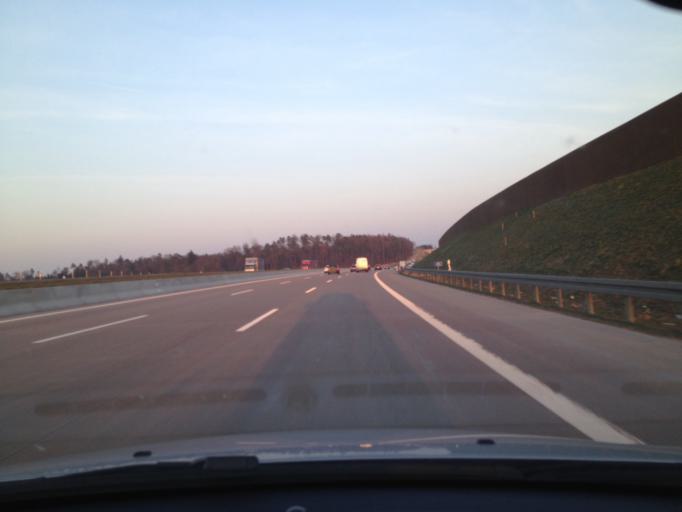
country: DE
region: Bavaria
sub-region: Swabia
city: Horgau
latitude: 48.4198
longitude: 10.6807
